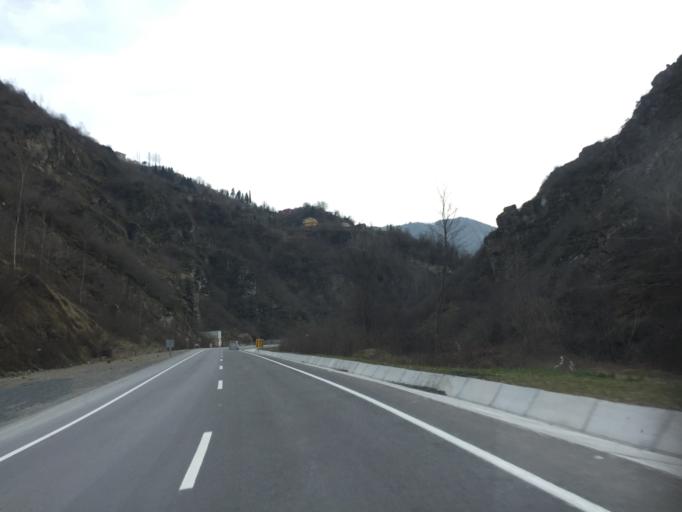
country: TR
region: Trabzon
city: Macka
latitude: 40.7697
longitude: 39.5652
